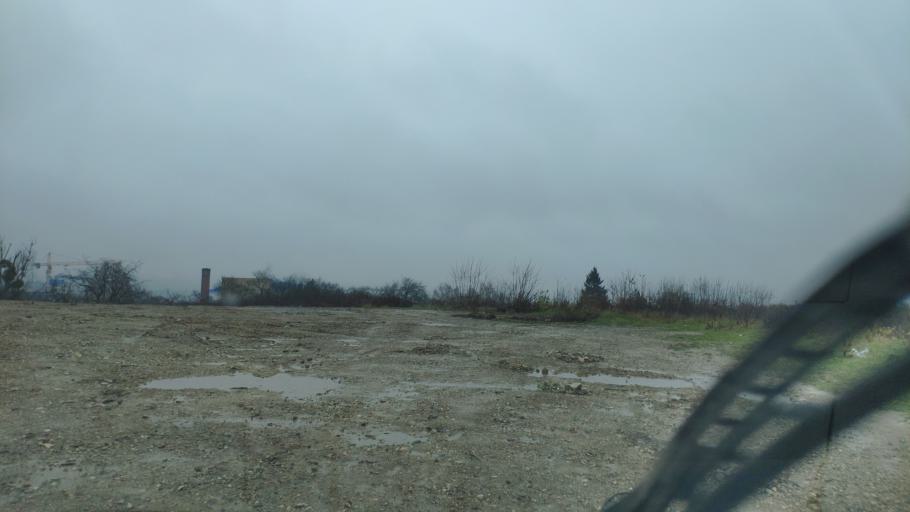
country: SK
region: Kosicky
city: Kosice
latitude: 48.7154
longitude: 21.2436
